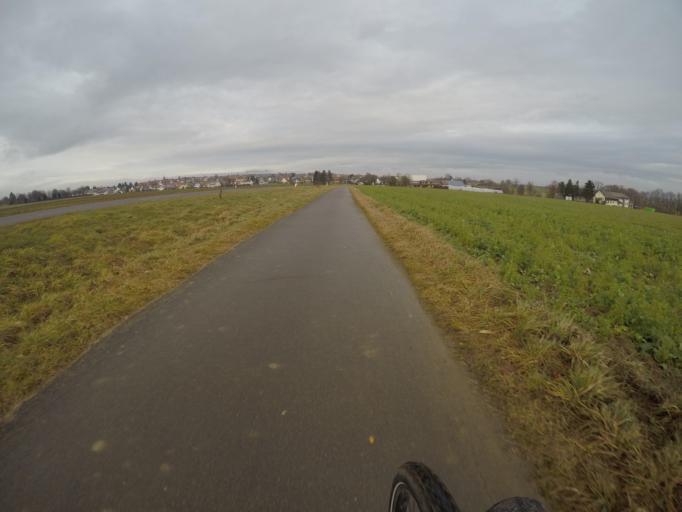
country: DE
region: Baden-Wuerttemberg
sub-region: Regierungsbezirk Stuttgart
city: Neckartailfingen
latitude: 48.6415
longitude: 9.2500
